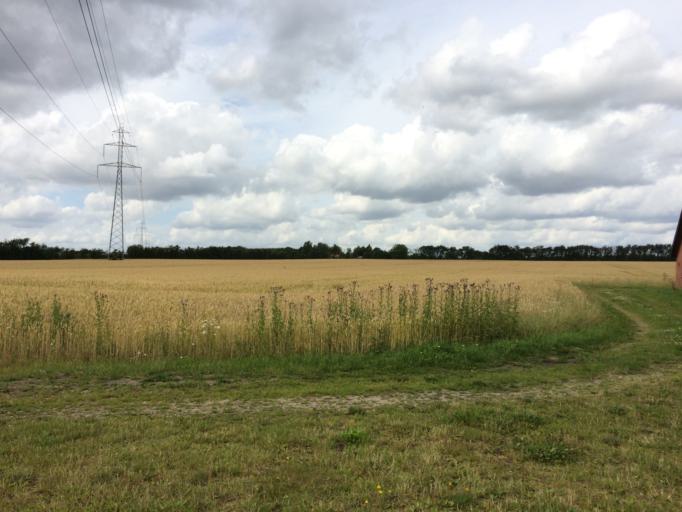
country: DK
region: Central Jutland
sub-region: Viborg Kommune
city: Viborg
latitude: 56.5004
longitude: 9.5251
